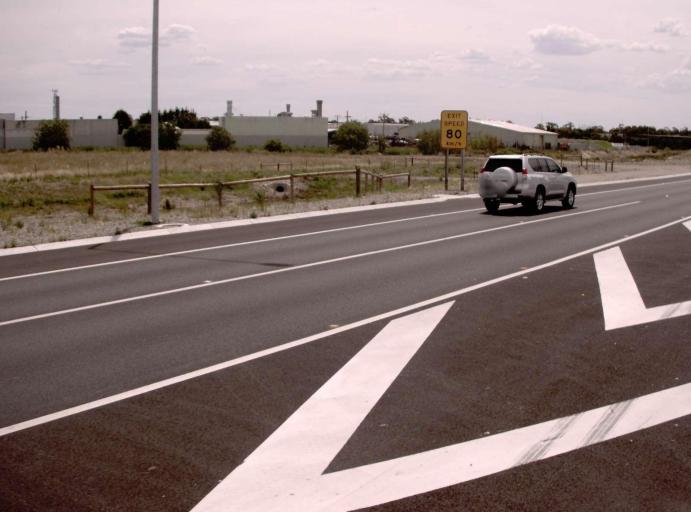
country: AU
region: Victoria
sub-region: Frankston
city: Carrum Downs
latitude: -38.0978
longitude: 145.1550
